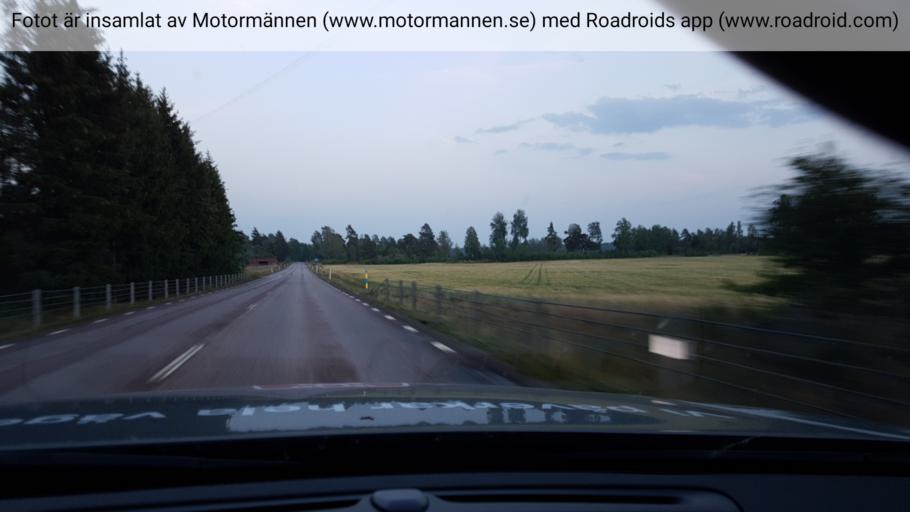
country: SE
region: Uppsala
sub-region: Heby Kommun
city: Heby
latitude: 59.8160
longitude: 16.7804
